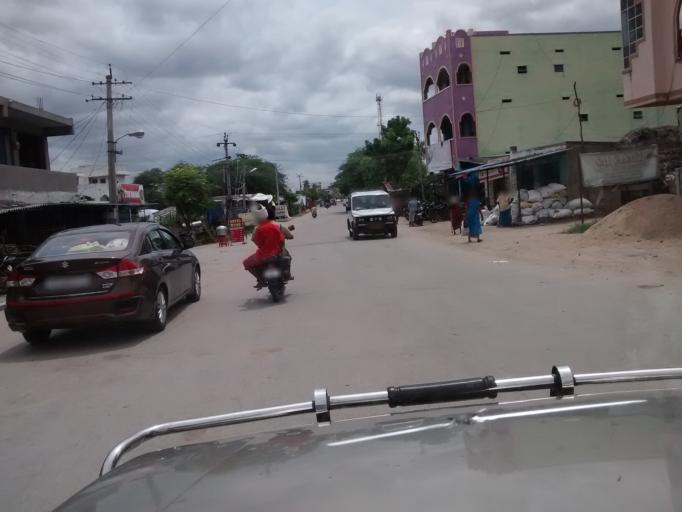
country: IN
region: Andhra Pradesh
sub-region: Chittoor
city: Chittoor
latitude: 13.2770
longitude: 79.0418
